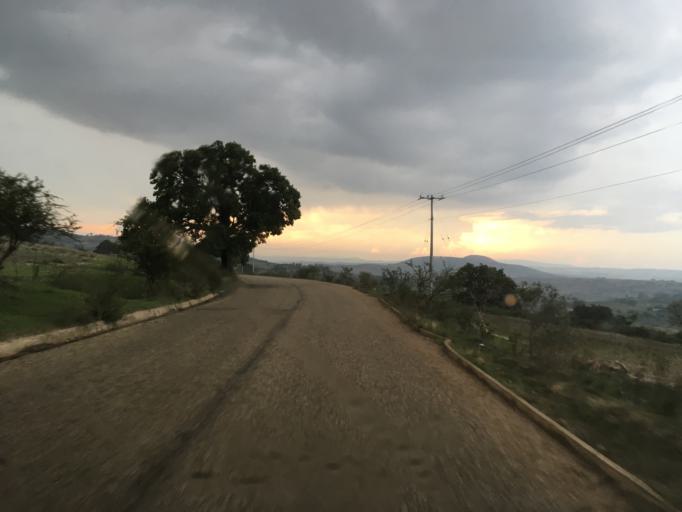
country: MX
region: Oaxaca
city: Santiago Tilantongo
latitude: 17.2789
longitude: -97.2914
